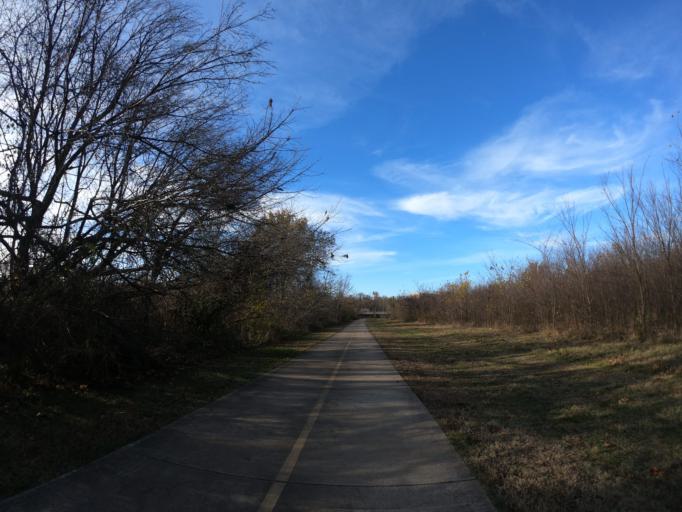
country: US
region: Arkansas
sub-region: Benton County
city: Cave Springs
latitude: 36.3031
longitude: -94.1795
